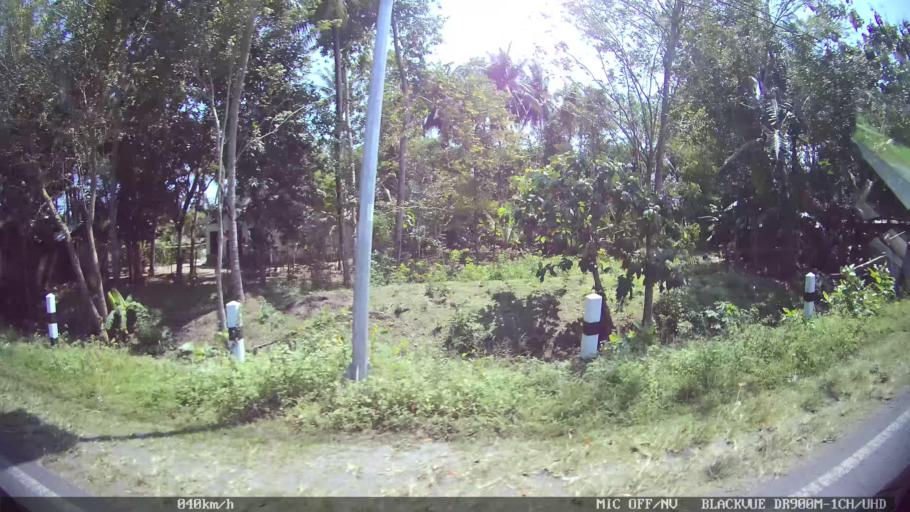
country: ID
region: Daerah Istimewa Yogyakarta
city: Srandakan
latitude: -7.9506
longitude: 110.2167
